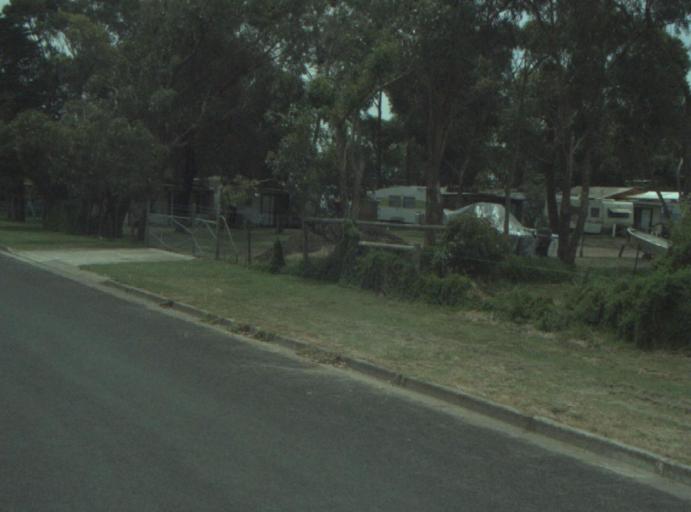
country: AU
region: Victoria
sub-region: Greater Geelong
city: Clifton Springs
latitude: -38.1164
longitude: 144.6698
